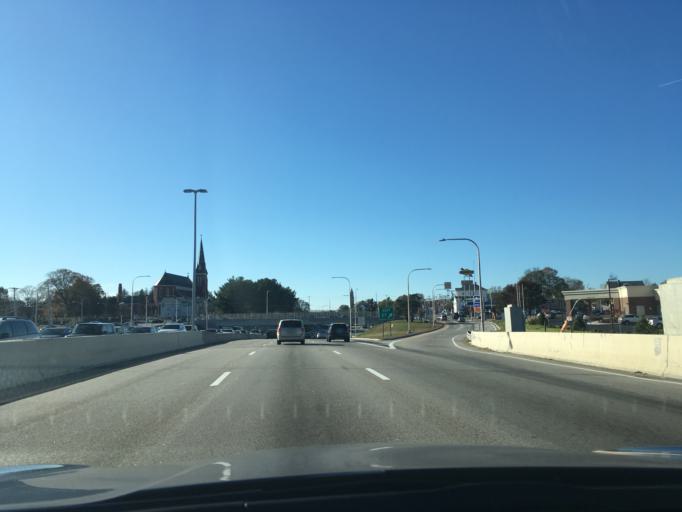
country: US
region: Rhode Island
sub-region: Providence County
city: Pawtucket
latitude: 41.8734
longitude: -71.3849
